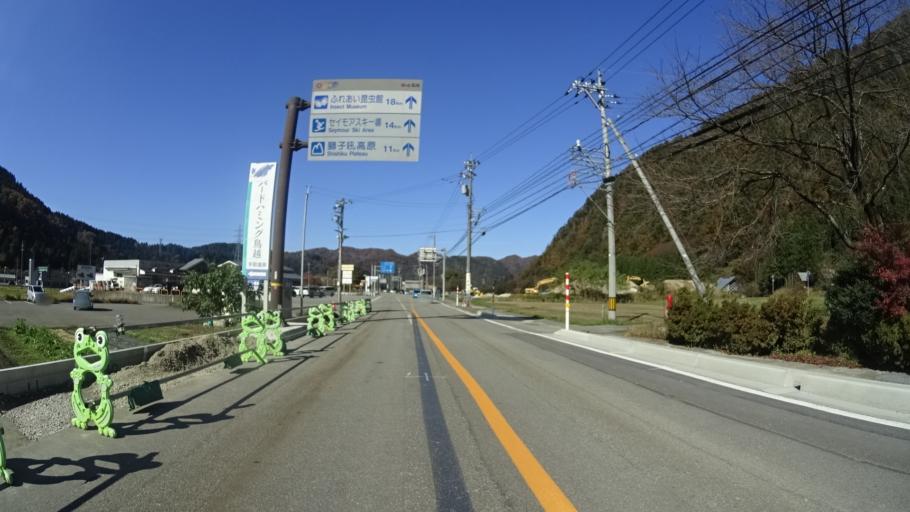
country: JP
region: Ishikawa
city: Tsurugi-asahimachi
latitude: 36.3622
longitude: 136.6180
